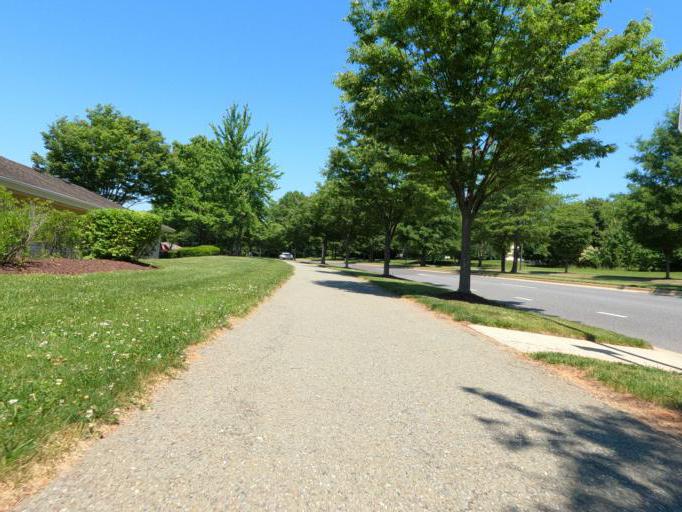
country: US
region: Maryland
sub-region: Montgomery County
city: Germantown
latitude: 39.2031
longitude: -77.2547
